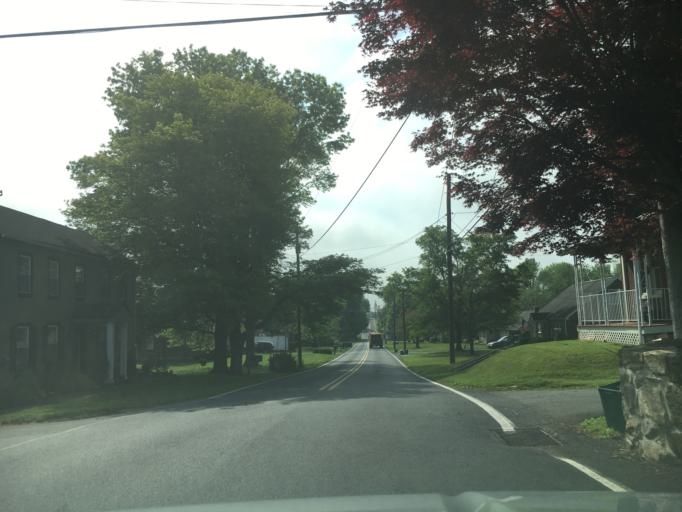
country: US
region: Pennsylvania
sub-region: Berks County
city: New Berlinville
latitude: 40.3454
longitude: -75.6332
